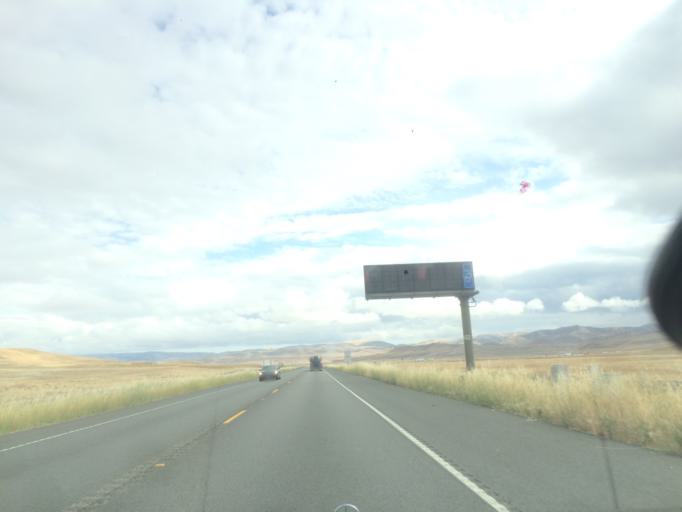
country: US
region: California
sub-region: San Luis Obispo County
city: Shandon
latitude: 35.7270
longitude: -120.2946
